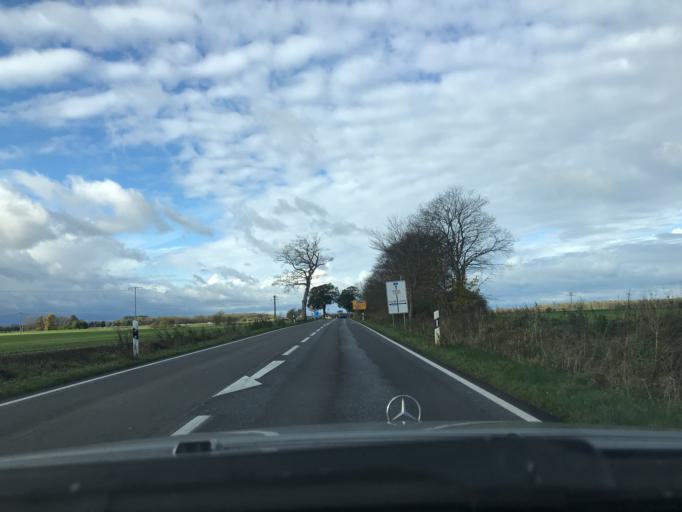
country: DE
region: Mecklenburg-Vorpommern
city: Jarmen
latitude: 53.9457
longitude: 13.3807
